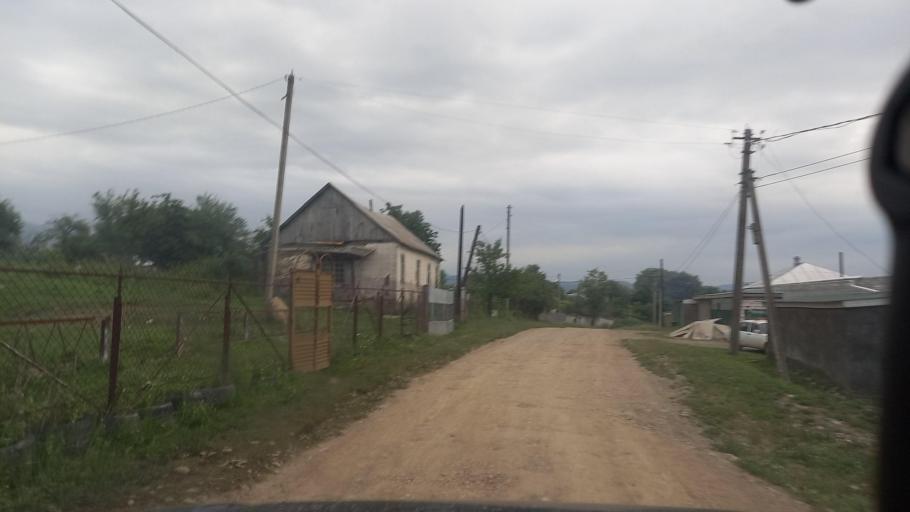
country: RU
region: Karachayevo-Cherkesiya
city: Pregradnaya
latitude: 43.9510
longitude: 41.1799
